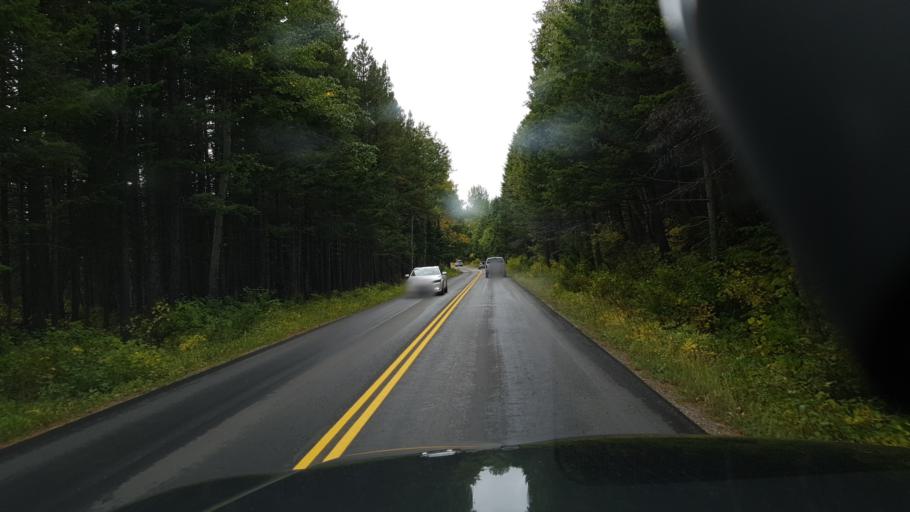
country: CA
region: Alberta
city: Cardston
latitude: 48.6756
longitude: -113.6328
